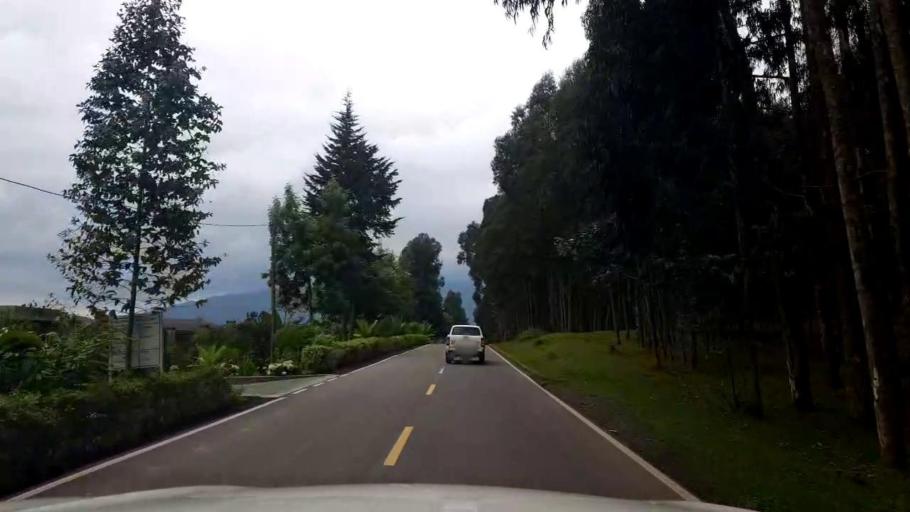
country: RW
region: Northern Province
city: Musanze
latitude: -1.4328
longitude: 29.5584
